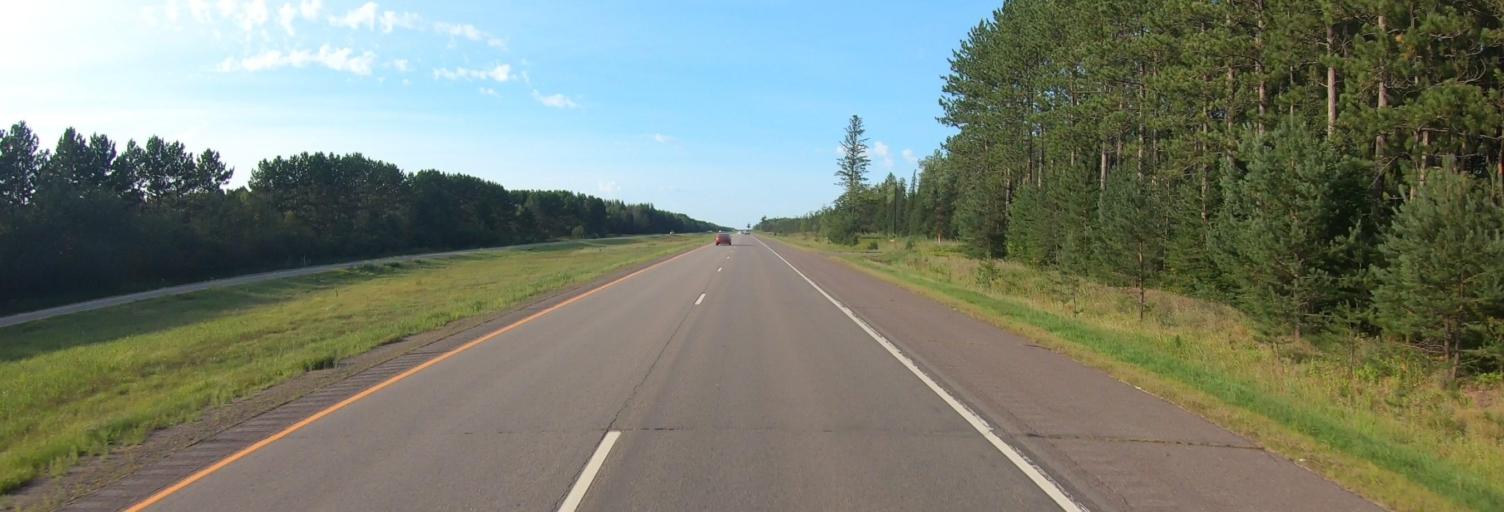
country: US
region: Minnesota
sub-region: Saint Louis County
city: Hermantown
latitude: 47.0898
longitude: -92.4714
